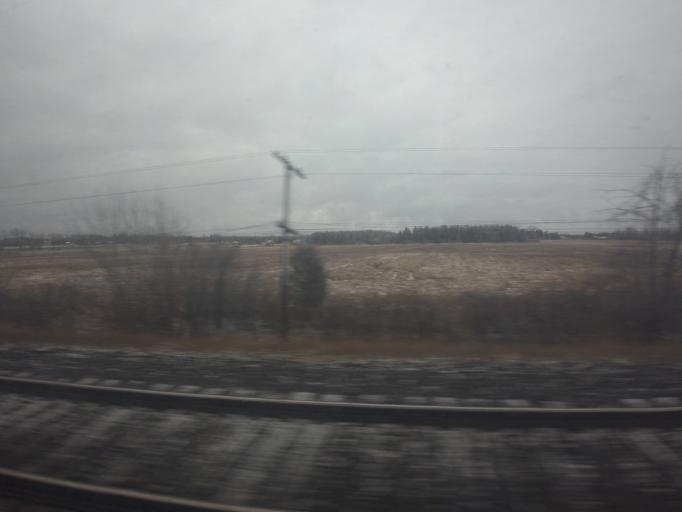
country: CA
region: Ontario
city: Gananoque
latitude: 44.3777
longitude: -76.0806
